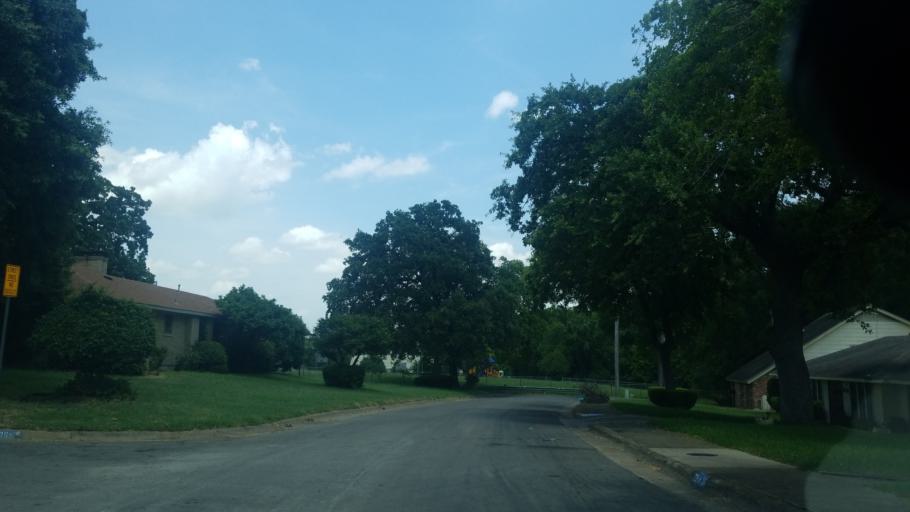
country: US
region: Texas
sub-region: Dallas County
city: Dallas
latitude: 32.7208
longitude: -96.7751
